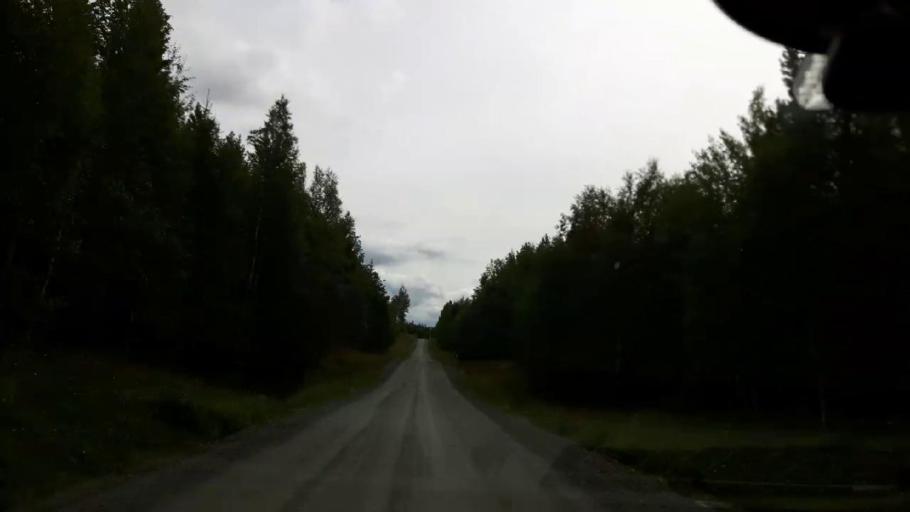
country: SE
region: Jaemtland
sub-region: Krokoms Kommun
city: Valla
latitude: 63.6550
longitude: 13.9790
